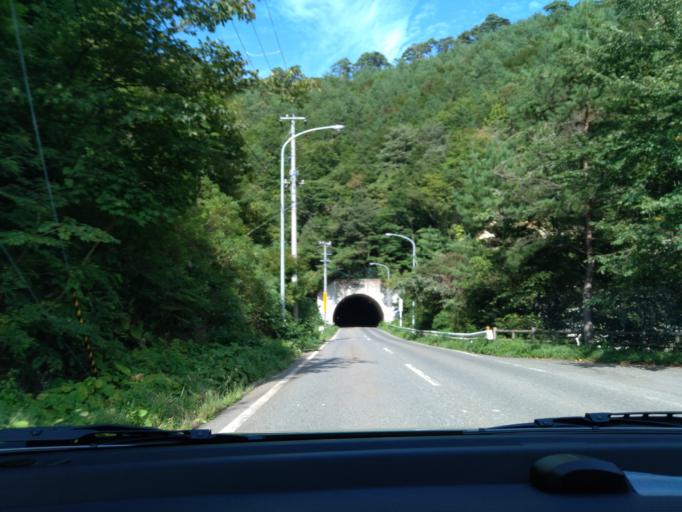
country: JP
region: Iwate
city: Shizukuishi
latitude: 39.6270
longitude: 141.0679
